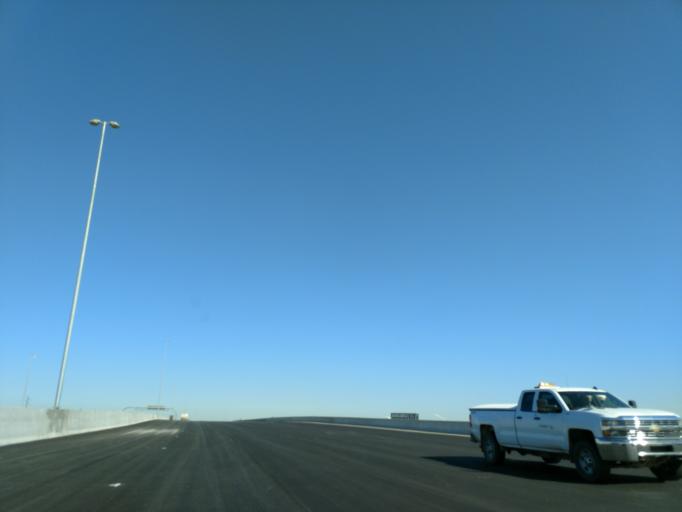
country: US
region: Arizona
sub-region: Maricopa County
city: Tolleson
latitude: 33.4495
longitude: -112.1858
